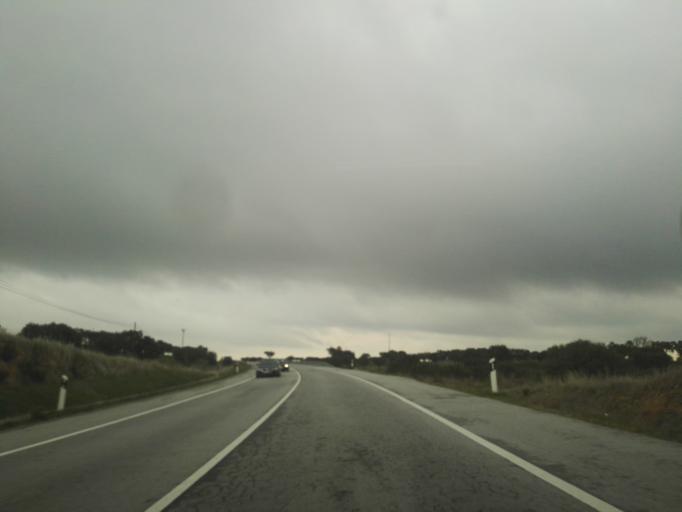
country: PT
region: Portalegre
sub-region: Portalegre
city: Urra
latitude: 39.2101
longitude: -7.3762
